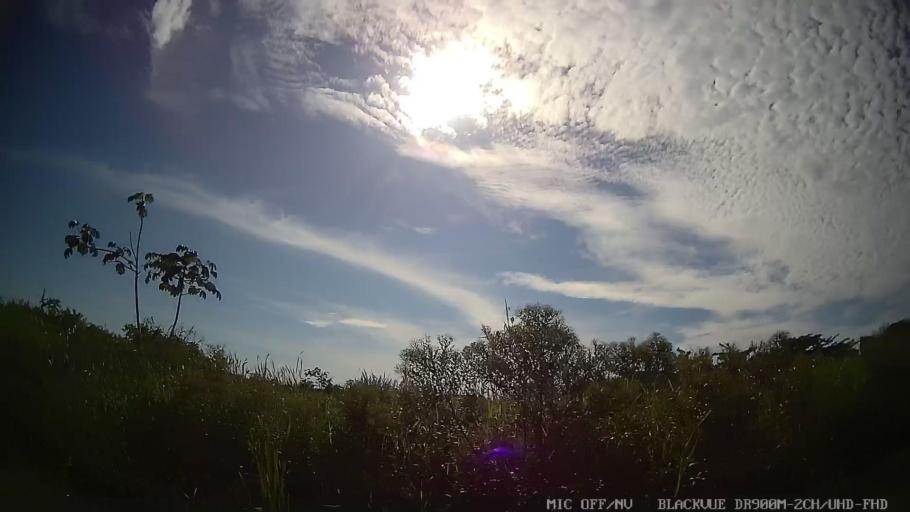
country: BR
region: Sao Paulo
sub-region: Iguape
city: Iguape
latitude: -24.7668
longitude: -47.5860
